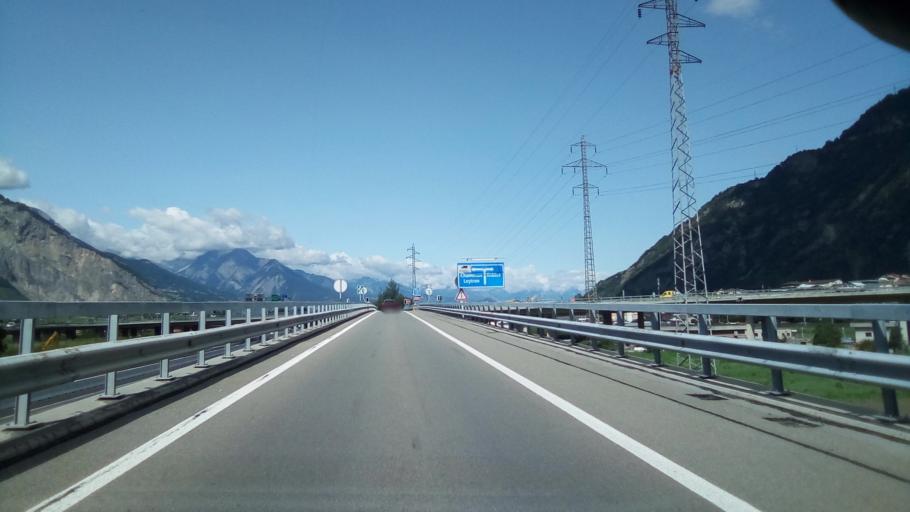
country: CH
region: Valais
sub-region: Martigny District
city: Riddes
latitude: 46.1711
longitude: 7.2124
